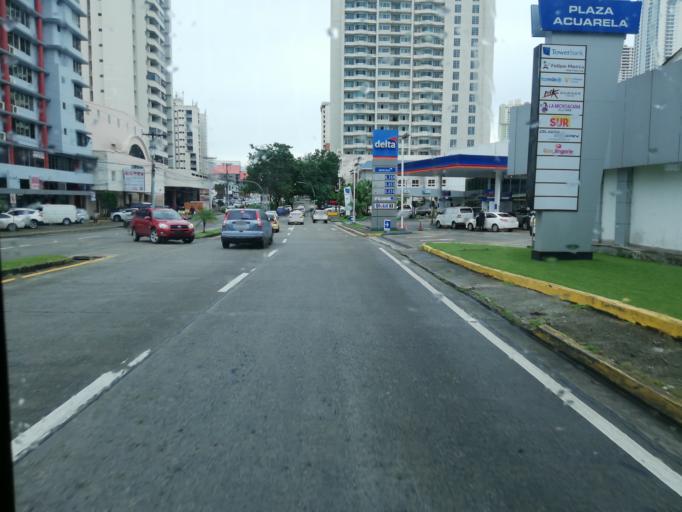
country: PA
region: Panama
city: Panama
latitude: 9.0060
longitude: -79.5405
